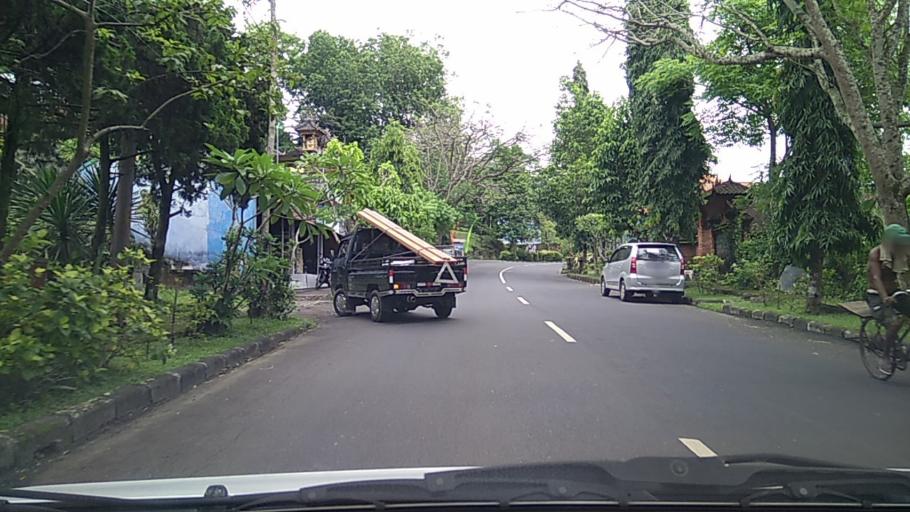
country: ID
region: Bali
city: Banjar Kelodan
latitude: -8.5252
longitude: 115.3468
